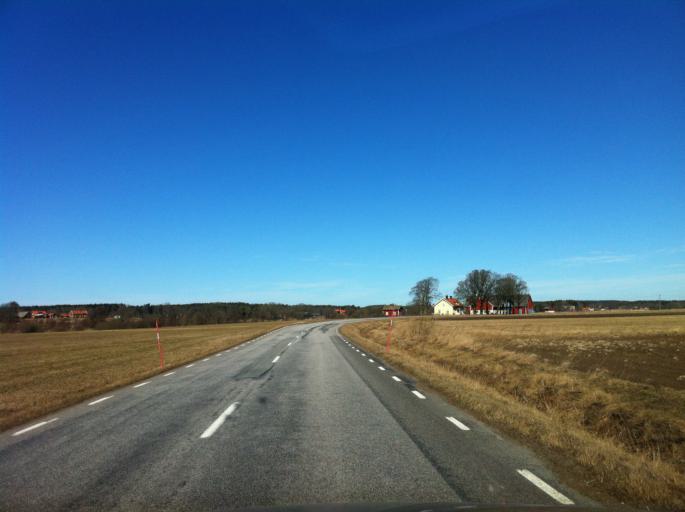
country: SE
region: Vaestra Goetaland
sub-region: Toreboda Kommun
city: Toereboda
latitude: 58.7071
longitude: 14.1282
